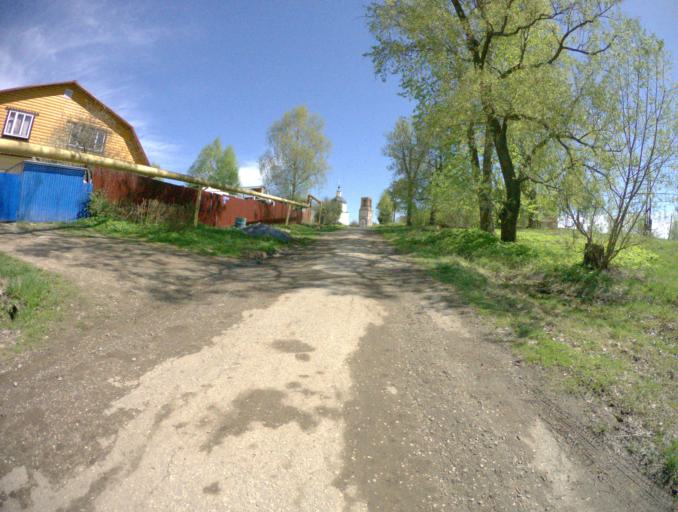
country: RU
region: Vladimir
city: Orgtrud
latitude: 56.2075
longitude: 40.5807
